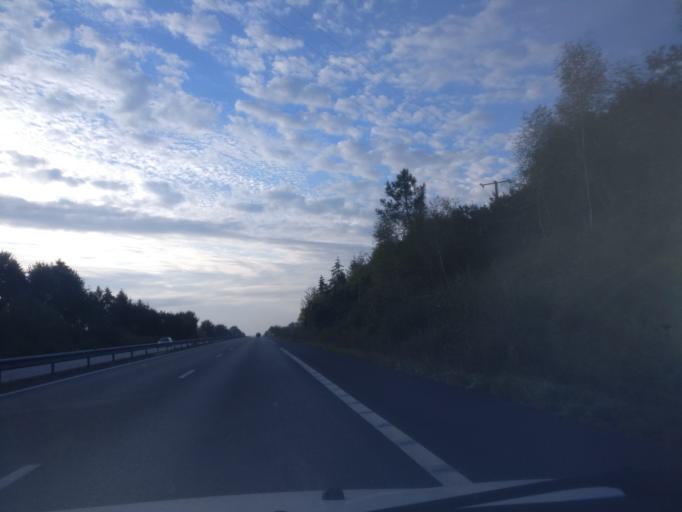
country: FR
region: Pays de la Loire
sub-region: Departement de la Loire-Atlantique
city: Derval
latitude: 47.6757
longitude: -1.6912
